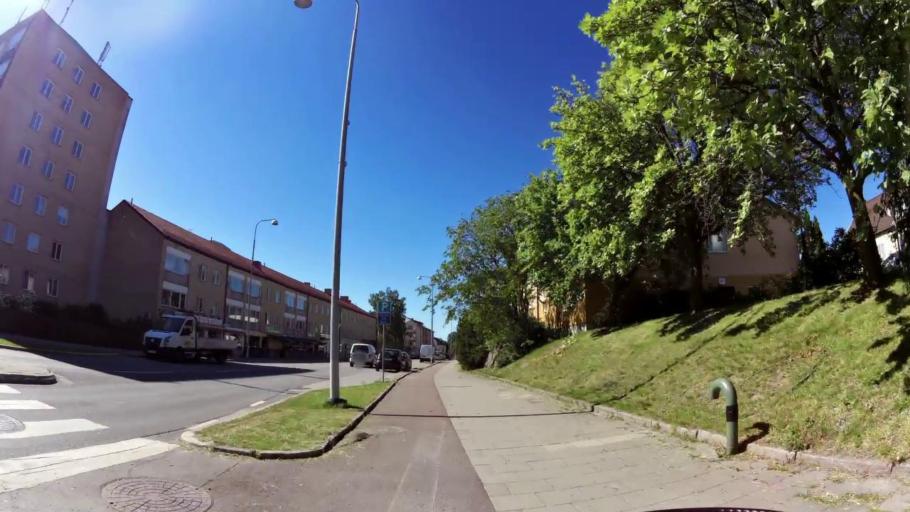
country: SE
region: OEstergoetland
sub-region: Linkopings Kommun
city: Linkoping
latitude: 58.4048
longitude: 15.6443
